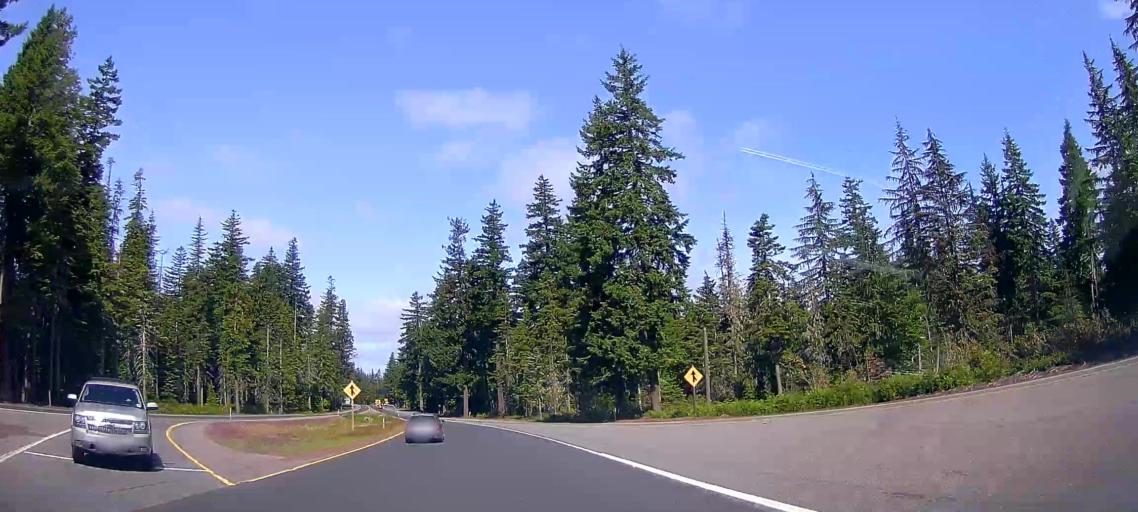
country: US
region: Oregon
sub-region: Clackamas County
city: Mount Hood Village
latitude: 45.1312
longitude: -121.6017
